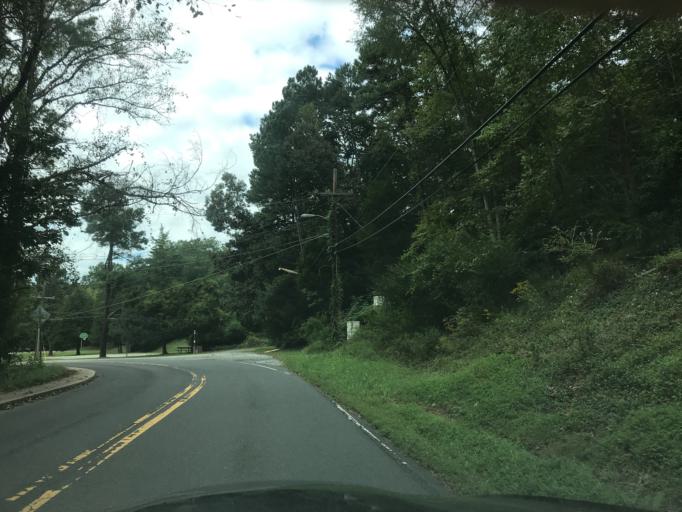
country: US
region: North Carolina
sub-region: Orange County
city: Chapel Hill
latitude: 35.9223
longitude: -79.0643
